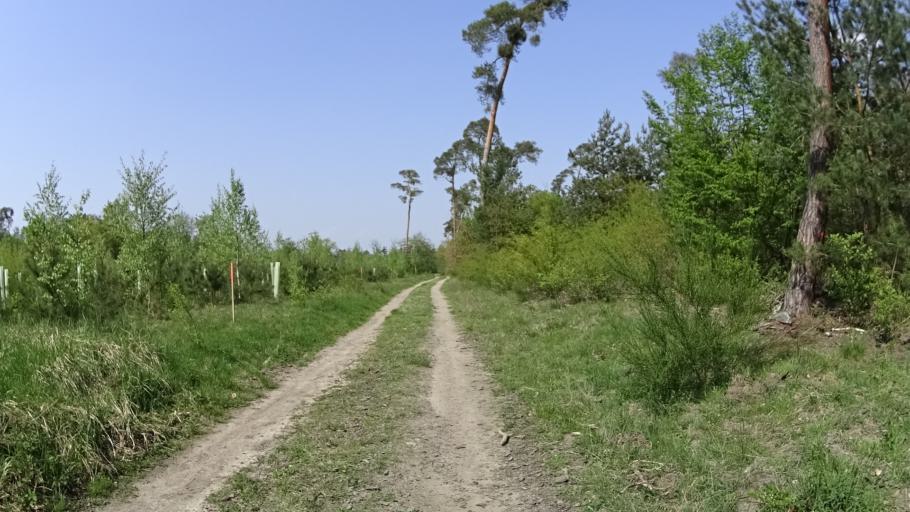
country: DE
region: Hesse
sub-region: Regierungsbezirk Darmstadt
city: Burstadt
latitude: 49.6522
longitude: 8.5059
